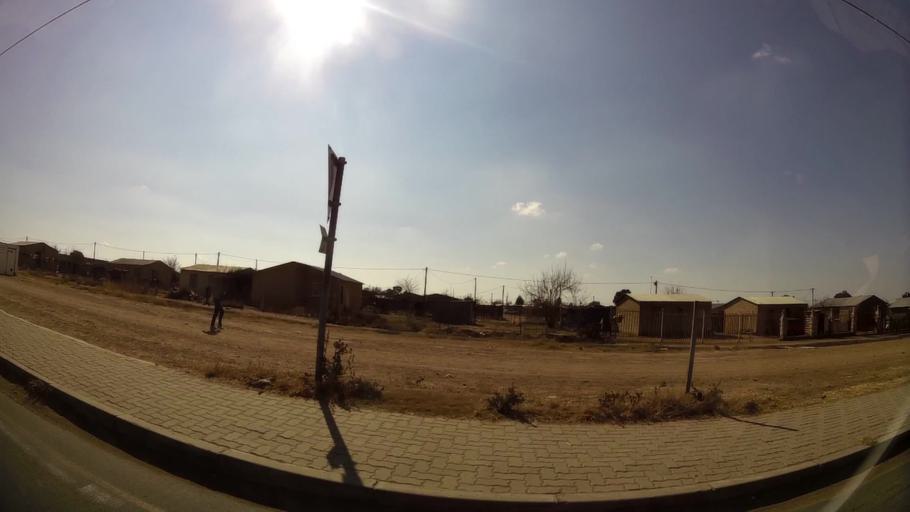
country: ZA
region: Orange Free State
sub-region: Mangaung Metropolitan Municipality
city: Bloemfontein
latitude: -29.1665
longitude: 26.2858
